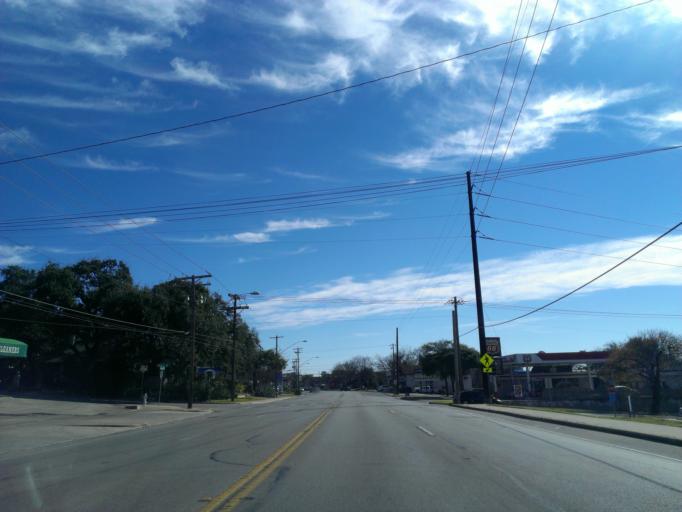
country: US
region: Texas
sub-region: Travis County
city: Rollingwood
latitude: 30.2789
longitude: -97.7738
